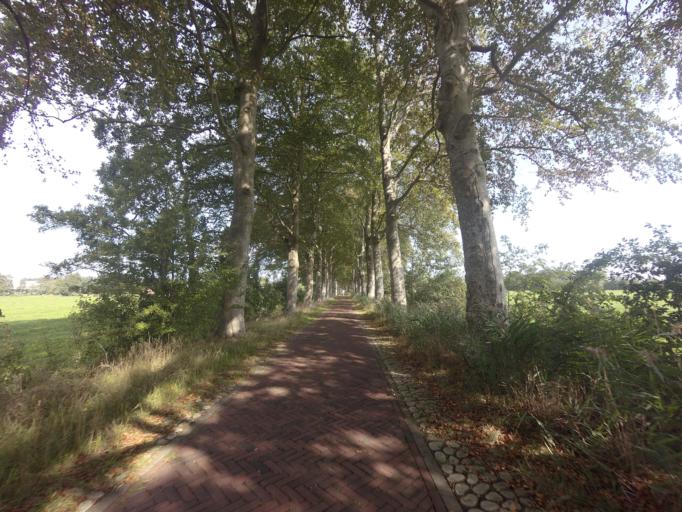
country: NL
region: Groningen
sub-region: Gemeente Leek
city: Leek
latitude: 53.1765
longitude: 6.3922
